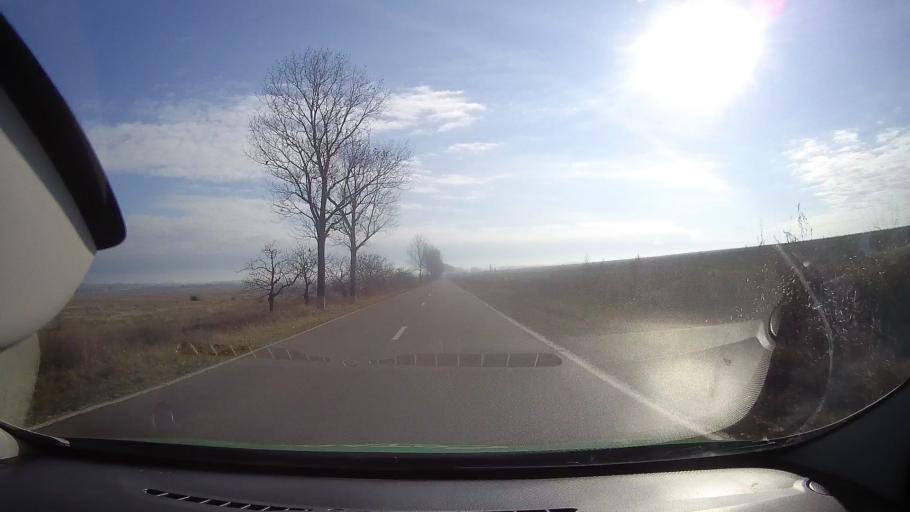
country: RO
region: Tulcea
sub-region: Comuna Mahmudia
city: Mahmudia
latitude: 45.0711
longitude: 29.0960
